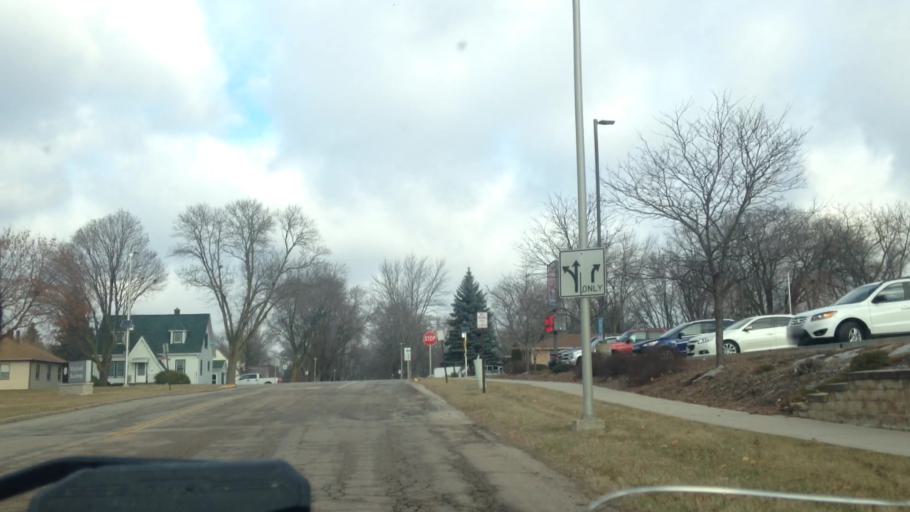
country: US
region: Wisconsin
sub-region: Dodge County
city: Beaver Dam
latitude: 43.4556
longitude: -88.8233
